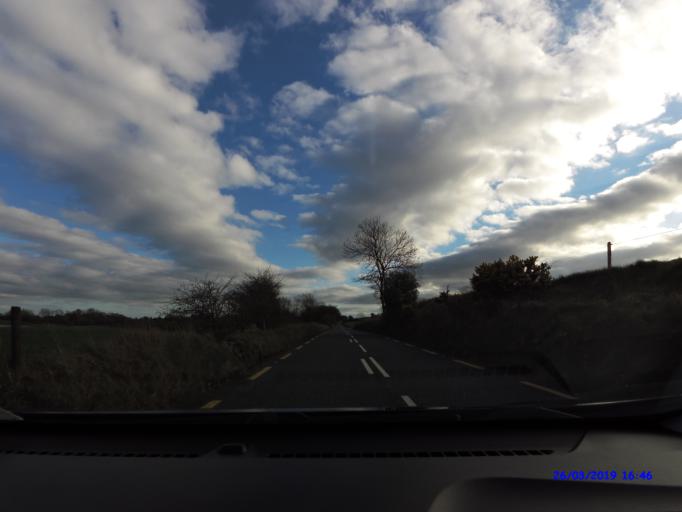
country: IE
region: Connaught
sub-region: Maigh Eo
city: Ballyhaunis
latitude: 53.8223
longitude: -8.7637
